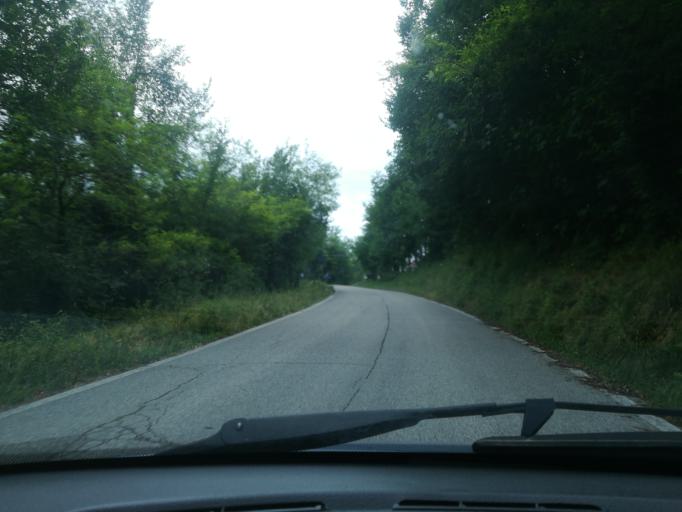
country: IT
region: The Marches
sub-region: Province of Fermo
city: Montefortino
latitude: 42.9405
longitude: 13.3722
